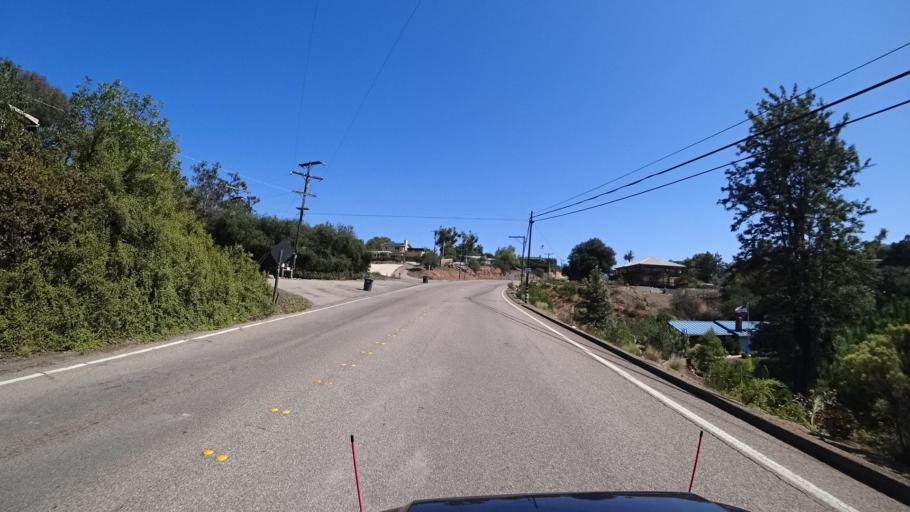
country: US
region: California
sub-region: San Diego County
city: Crest
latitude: 32.8149
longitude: -116.8648
